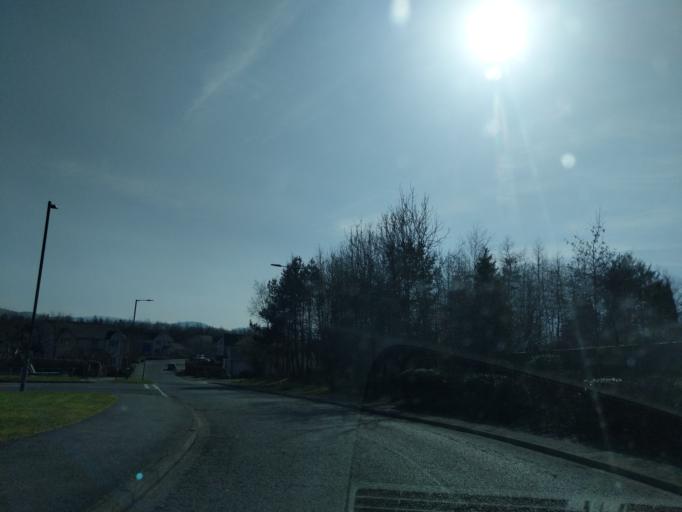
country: GB
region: Scotland
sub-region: The Scottish Borders
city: West Linton
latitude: 55.7557
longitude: -3.3489
